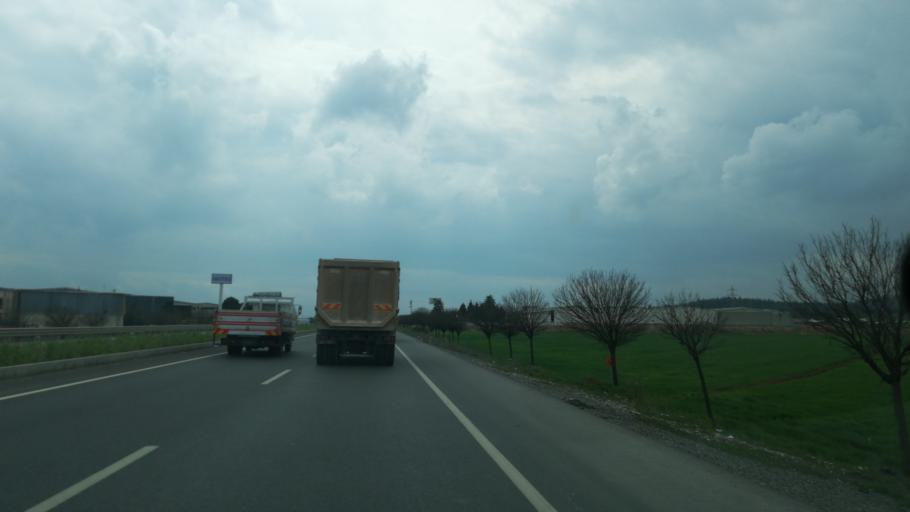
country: TR
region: Kahramanmaras
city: Turkoglu
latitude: 37.4366
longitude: 36.8857
